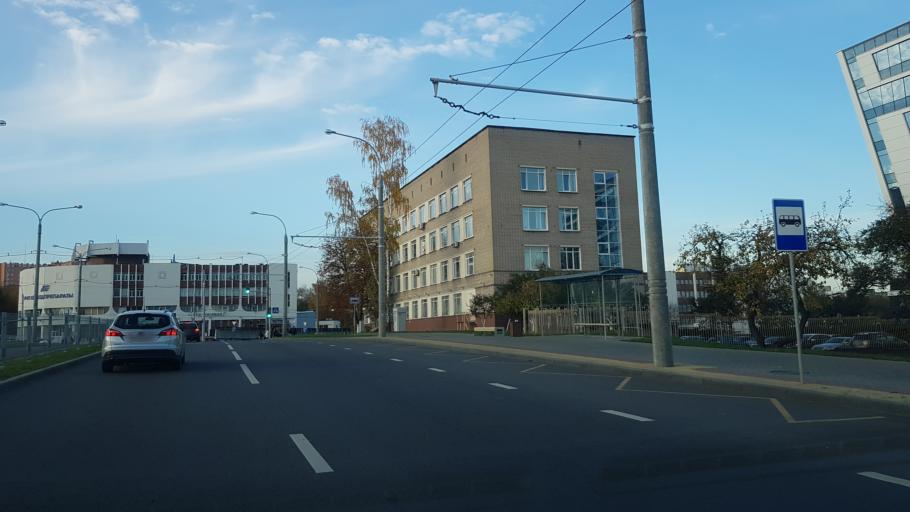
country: BY
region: Minsk
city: Minsk
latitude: 53.8847
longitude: 27.5684
